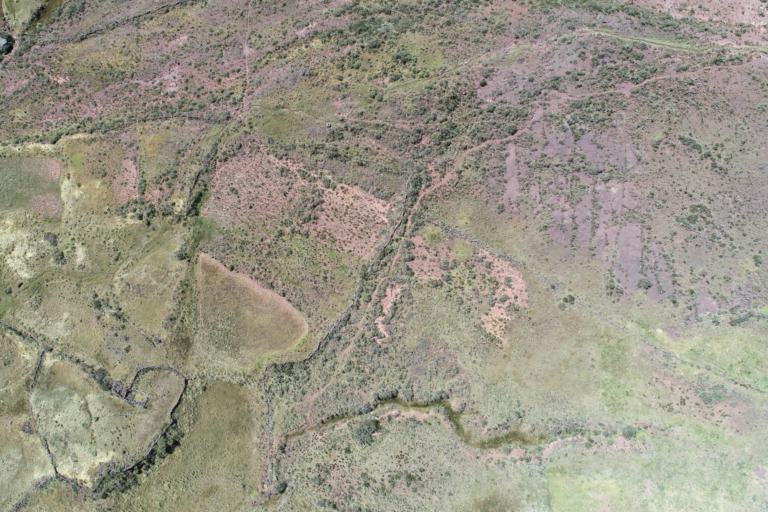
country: BO
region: La Paz
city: Tiahuanaco
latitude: -16.6076
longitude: -68.7618
